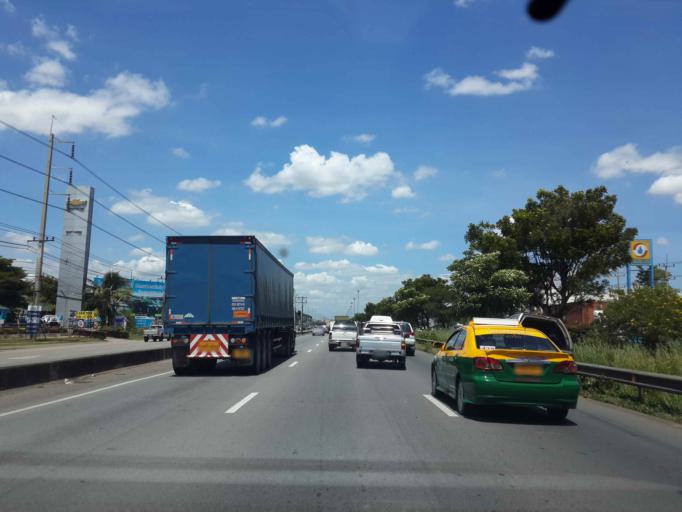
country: TH
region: Samut Sakhon
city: Samut Sakhon
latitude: 13.5779
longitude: 100.3031
